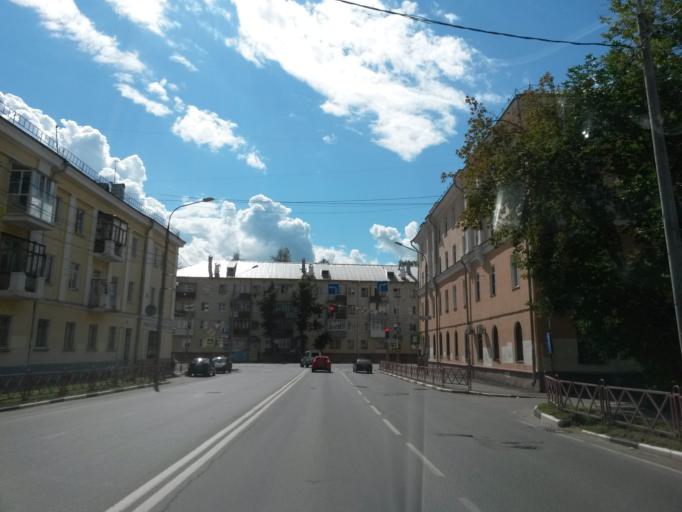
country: RU
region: Jaroslavl
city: Yaroslavl
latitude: 57.6222
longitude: 39.8681
